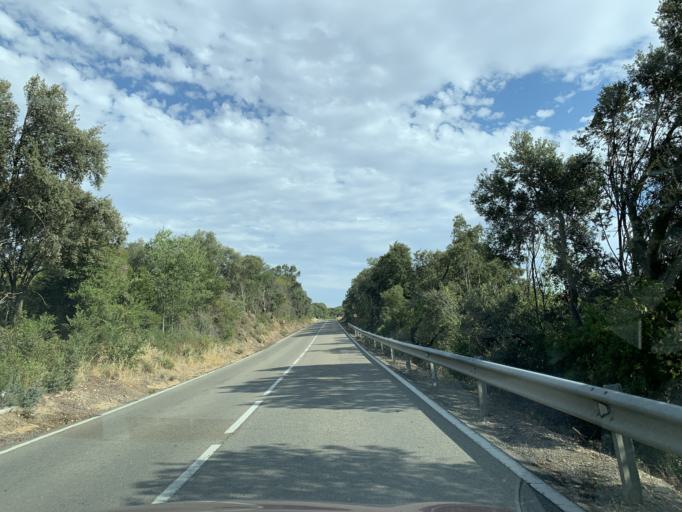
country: ES
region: Aragon
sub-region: Provincia de Zaragoza
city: Santa Eulalia de Gallego
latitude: 42.3081
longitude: -0.7475
